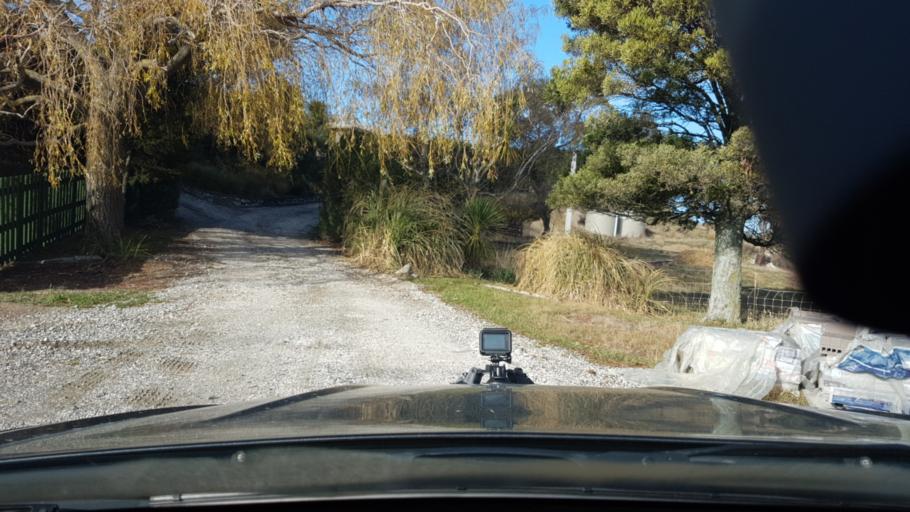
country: NZ
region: Marlborough
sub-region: Marlborough District
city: Blenheim
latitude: -41.8422
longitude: 174.1234
